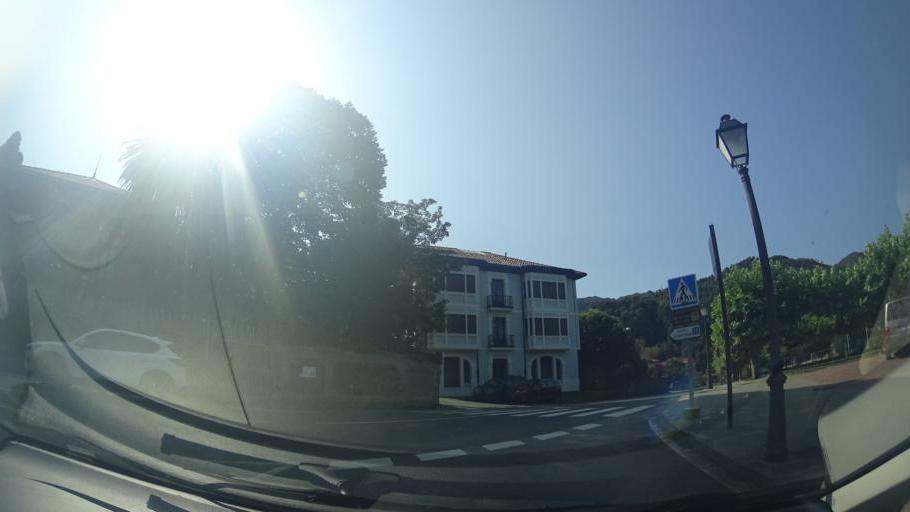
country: ES
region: Asturias
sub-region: Province of Asturias
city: Colunga
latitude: 43.4637
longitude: -5.1869
